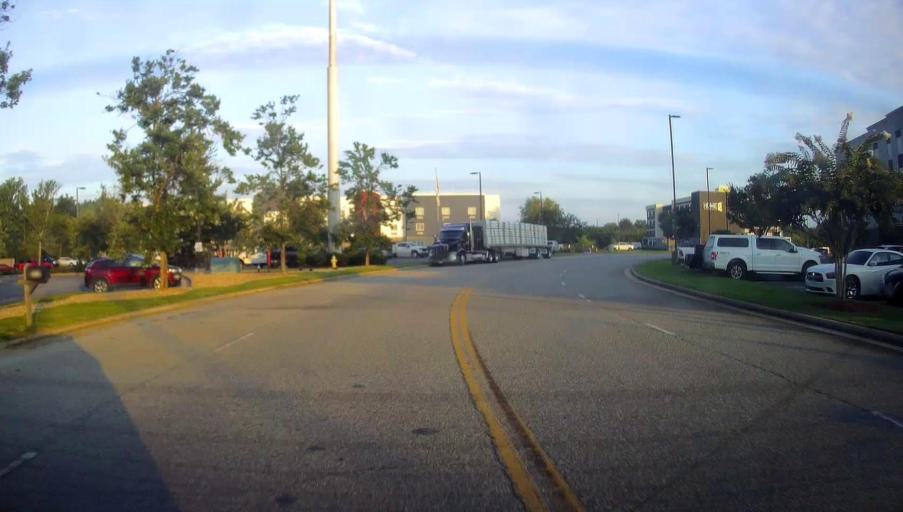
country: US
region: Georgia
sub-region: Bibb County
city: Macon
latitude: 32.9039
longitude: -83.6830
